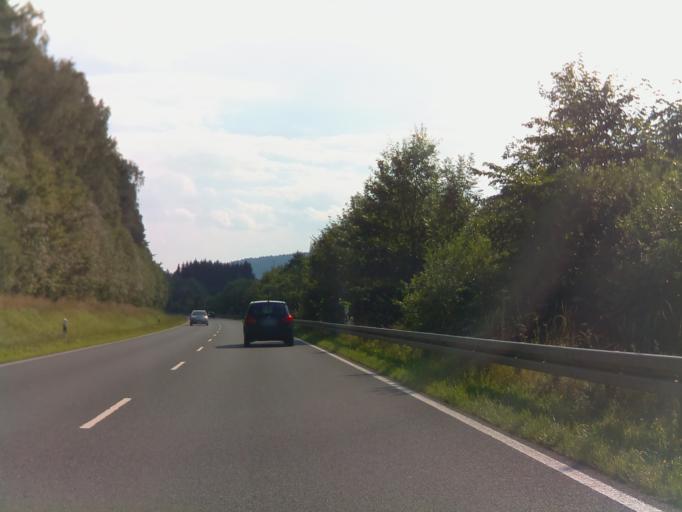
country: DE
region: Bavaria
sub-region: Regierungsbezirk Unterfranken
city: Wildflecken
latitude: 50.3704
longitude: 9.8994
